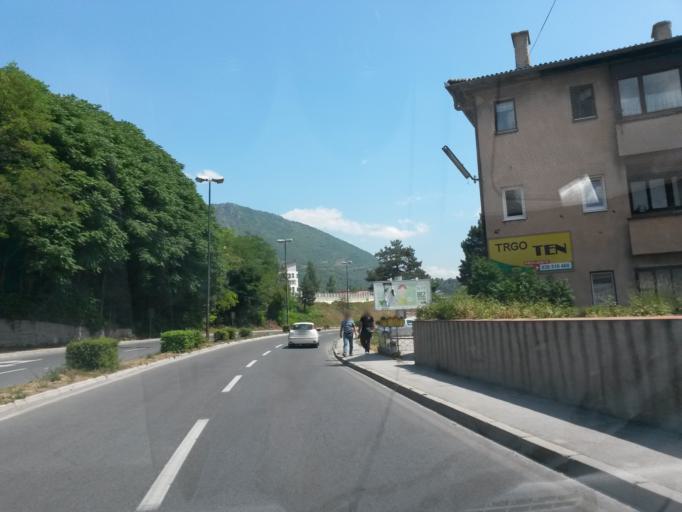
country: BA
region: Federation of Bosnia and Herzegovina
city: Travnik
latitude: 44.2277
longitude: 17.6592
